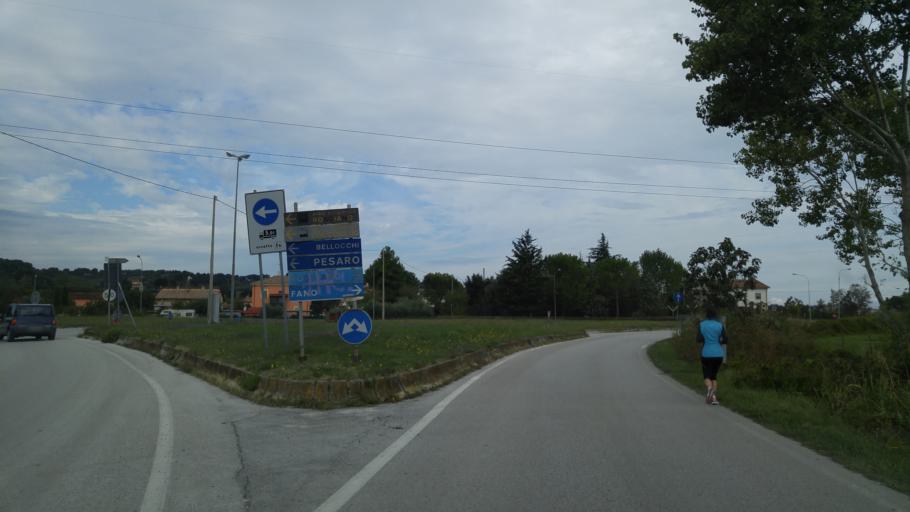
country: IT
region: The Marches
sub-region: Provincia di Pesaro e Urbino
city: Rosciano
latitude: 43.8156
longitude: 12.9996
